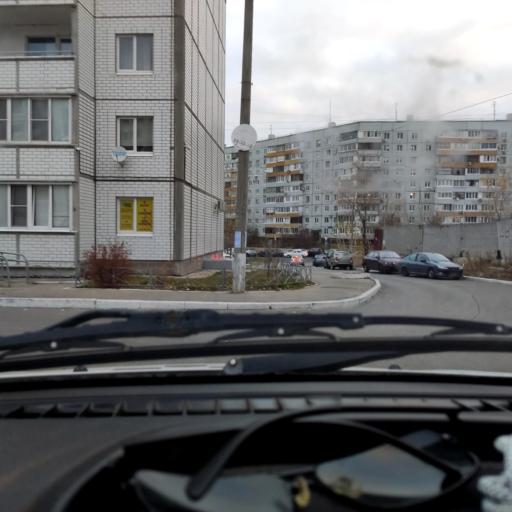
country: RU
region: Samara
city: Zhigulevsk
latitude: 53.4733
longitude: 49.5215
